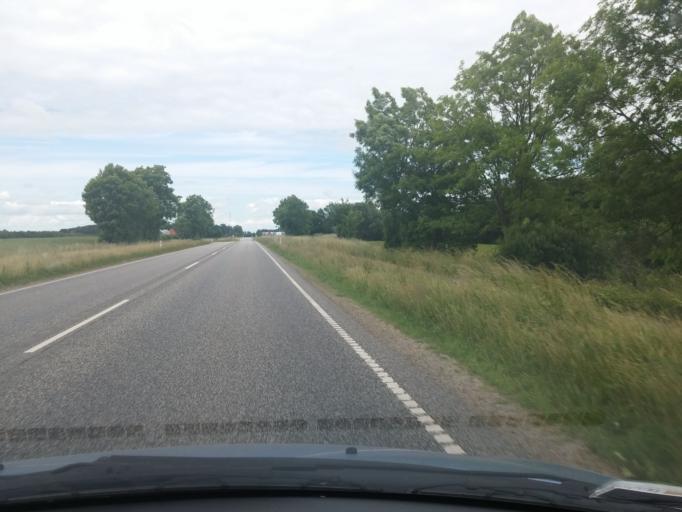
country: DK
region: South Denmark
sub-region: Haderslev Kommune
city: Haderslev
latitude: 55.2105
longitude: 9.4797
